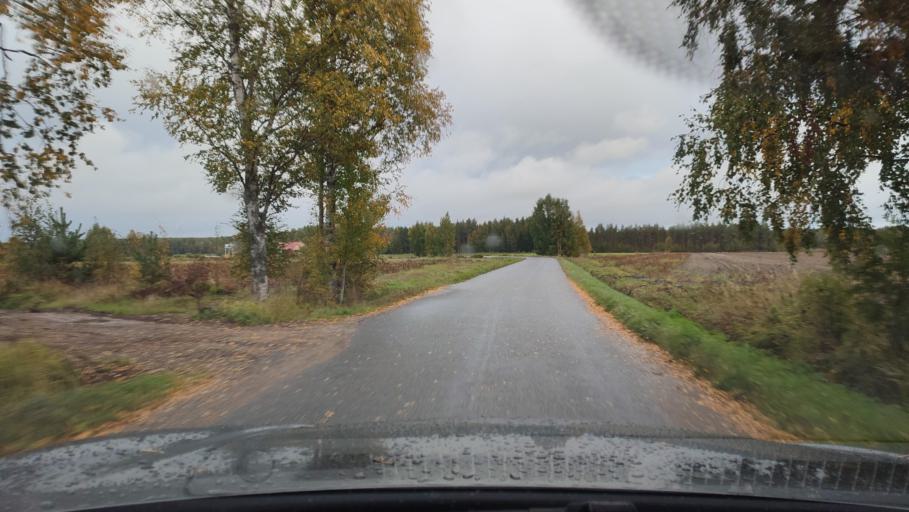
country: FI
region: Southern Ostrobothnia
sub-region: Suupohja
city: Karijoki
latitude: 62.2253
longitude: 21.6330
